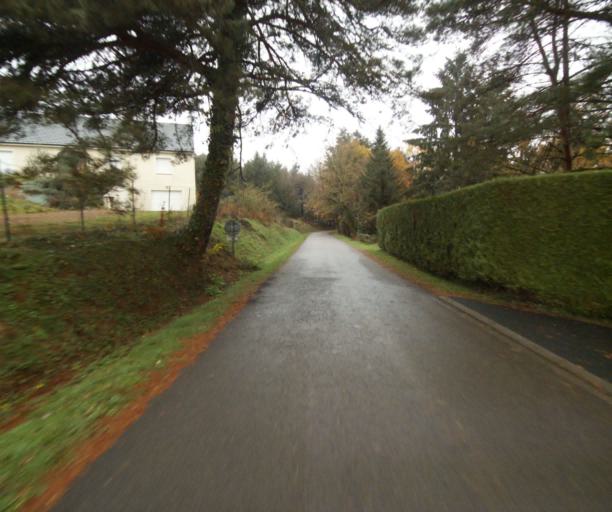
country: FR
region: Limousin
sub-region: Departement de la Correze
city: Cornil
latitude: 45.1953
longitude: 1.6424
